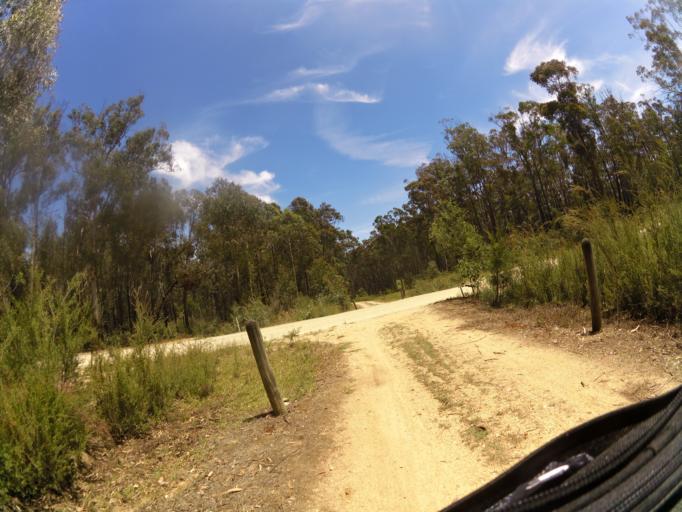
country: AU
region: Victoria
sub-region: East Gippsland
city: Lakes Entrance
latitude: -37.7584
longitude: 147.9439
